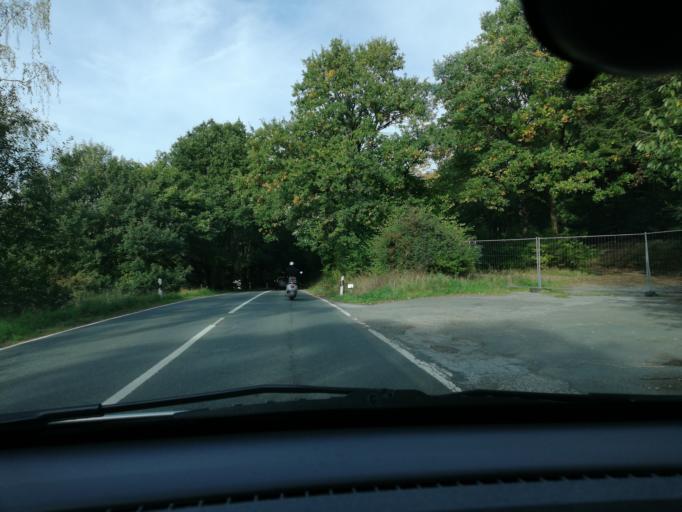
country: DE
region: North Rhine-Westphalia
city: Sprockhovel
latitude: 51.3491
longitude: 7.2527
